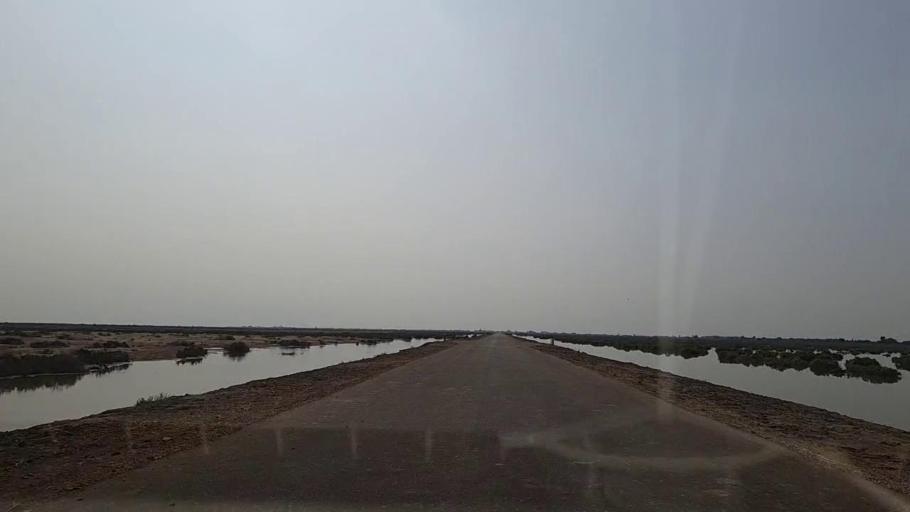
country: PK
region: Sindh
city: Chuhar Jamali
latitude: 24.2148
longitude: 67.8656
